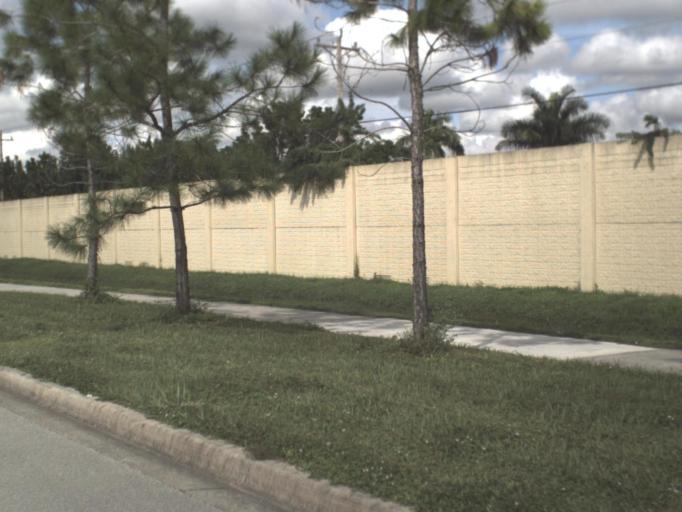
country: US
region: Florida
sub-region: Lee County
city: Palmona Park
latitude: 26.6931
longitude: -81.8881
